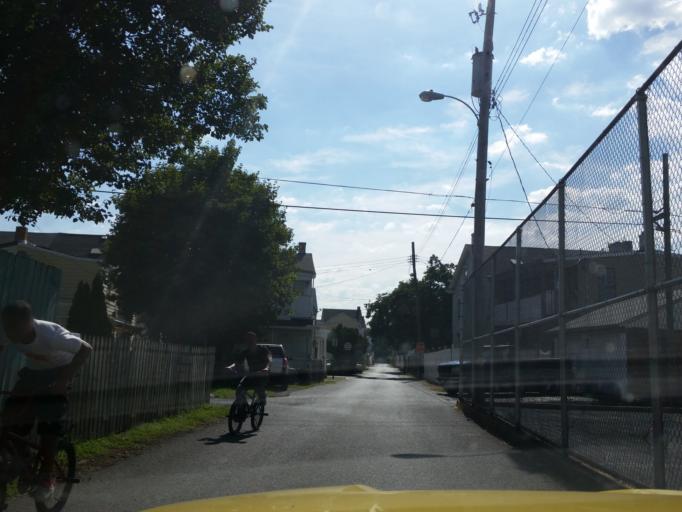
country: US
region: Pennsylvania
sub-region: Lebanon County
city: Lebanon
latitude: 40.3477
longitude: -76.4215
